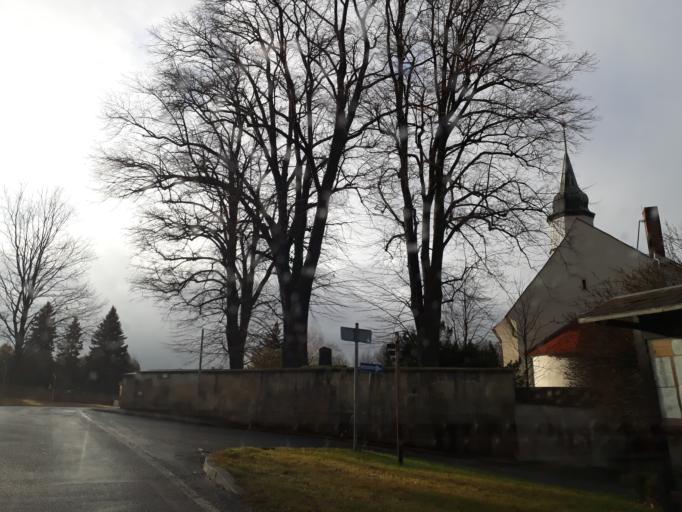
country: DE
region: Saxony
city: Herrnhut
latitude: 50.9977
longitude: 14.7228
